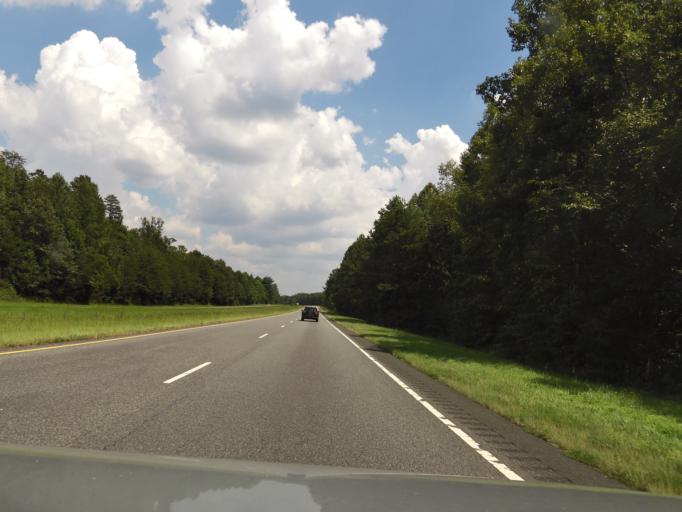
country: US
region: North Carolina
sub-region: Polk County
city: Columbus
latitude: 35.2712
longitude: -82.1457
